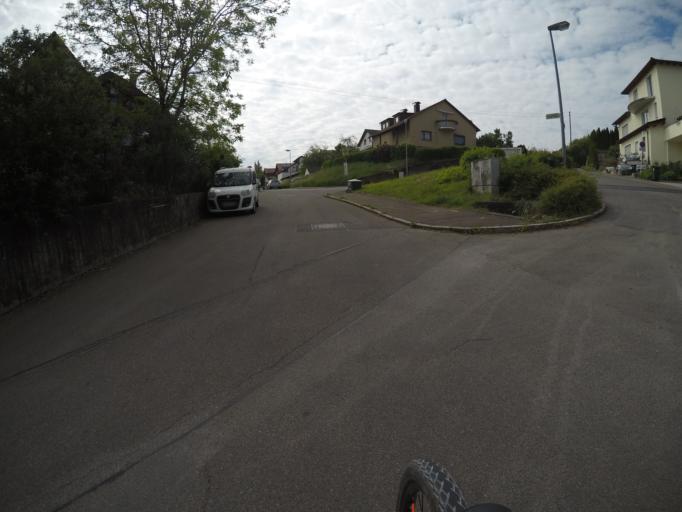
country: DE
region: Baden-Wuerttemberg
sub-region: Regierungsbezirk Stuttgart
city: Oberboihingen
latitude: 48.6458
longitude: 9.3723
